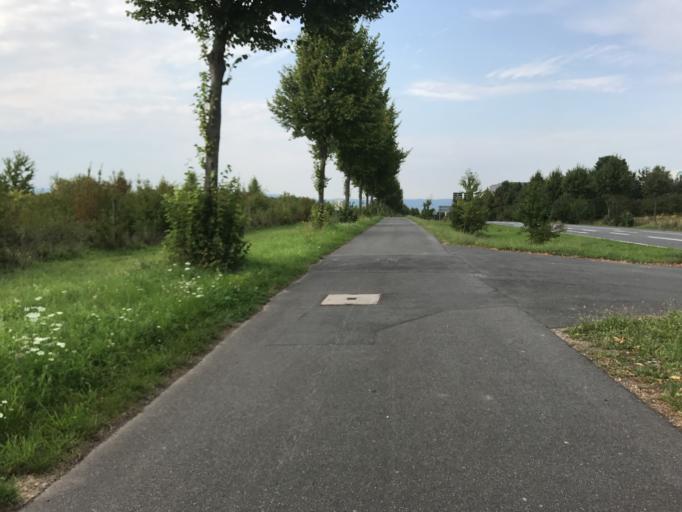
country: DE
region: Rheinland-Pfalz
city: Mainz
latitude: 49.9573
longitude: 8.2512
